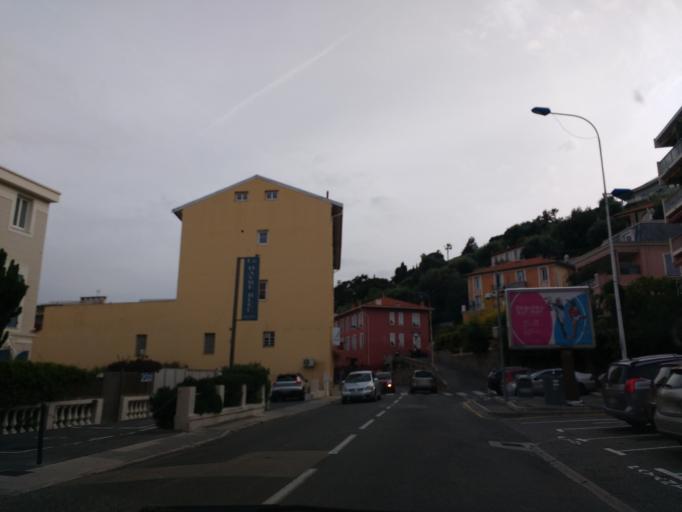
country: FR
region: Provence-Alpes-Cote d'Azur
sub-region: Departement des Alpes-Maritimes
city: Beaulieu-sur-Mer
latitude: 43.7058
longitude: 7.3273
